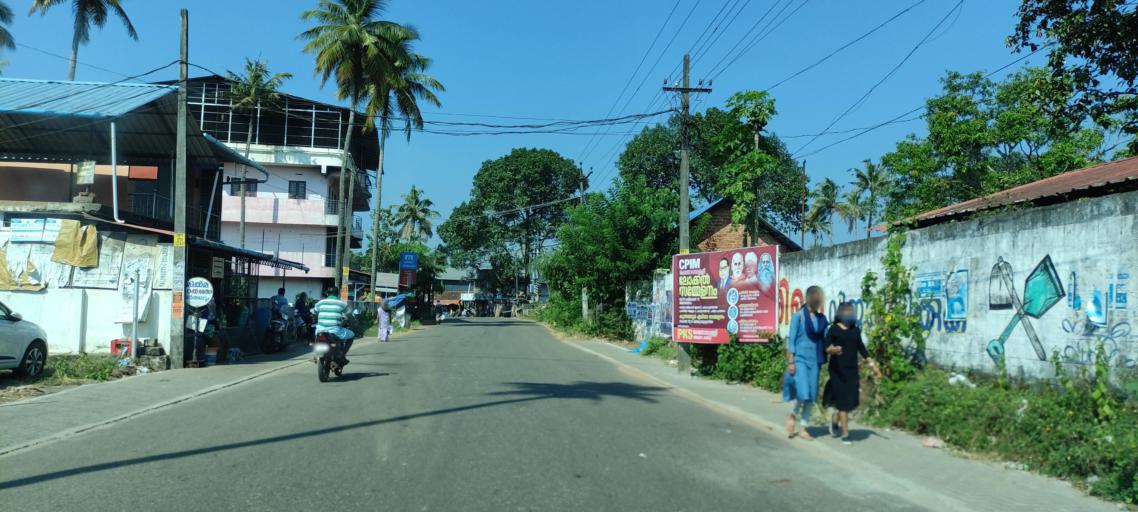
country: IN
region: Kerala
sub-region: Kollam
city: Panmana
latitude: 9.0430
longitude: 76.5816
